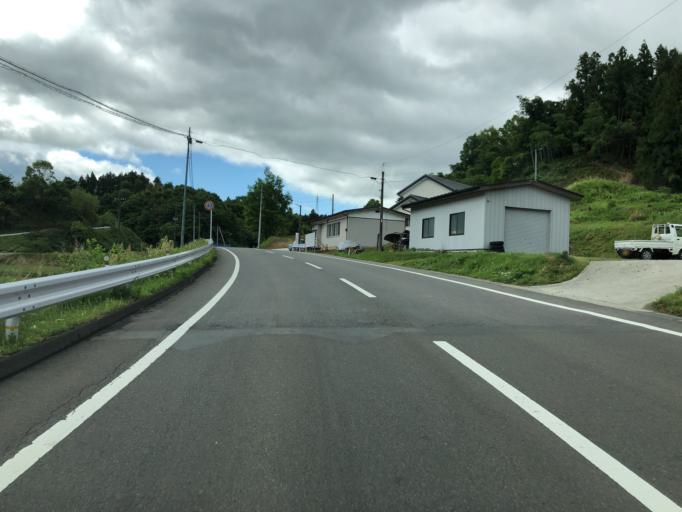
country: JP
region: Fukushima
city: Nihommatsu
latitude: 37.5477
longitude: 140.4596
